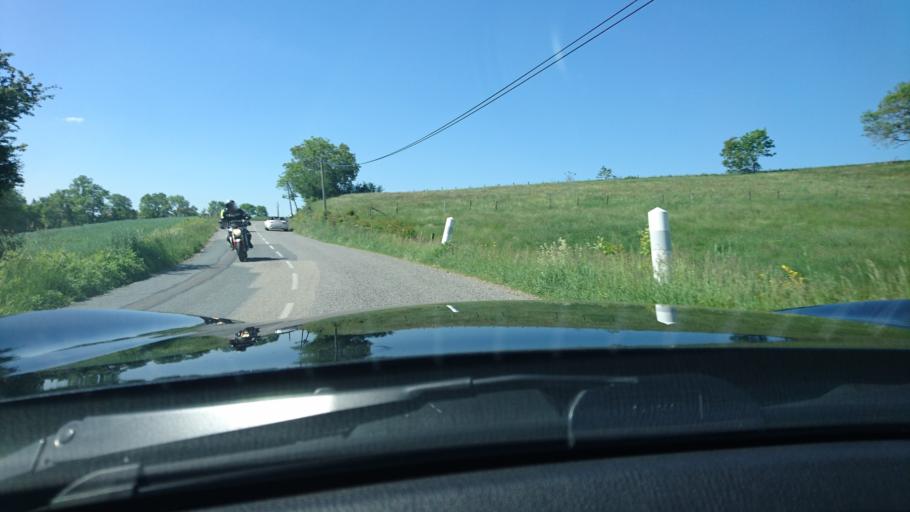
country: FR
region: Rhone-Alpes
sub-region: Departement du Rhone
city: Montrottier
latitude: 45.8109
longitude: 4.4160
